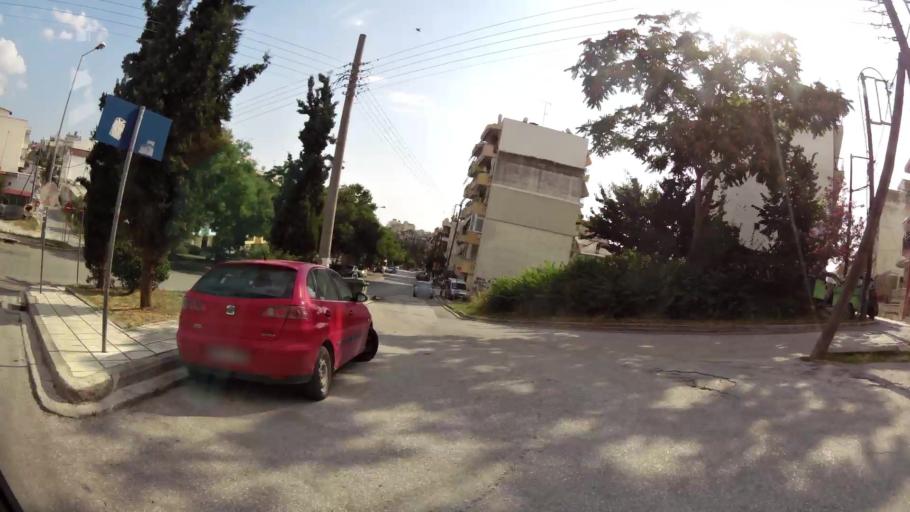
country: GR
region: Central Macedonia
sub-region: Nomos Thessalonikis
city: Polichni
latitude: 40.6611
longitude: 22.9516
